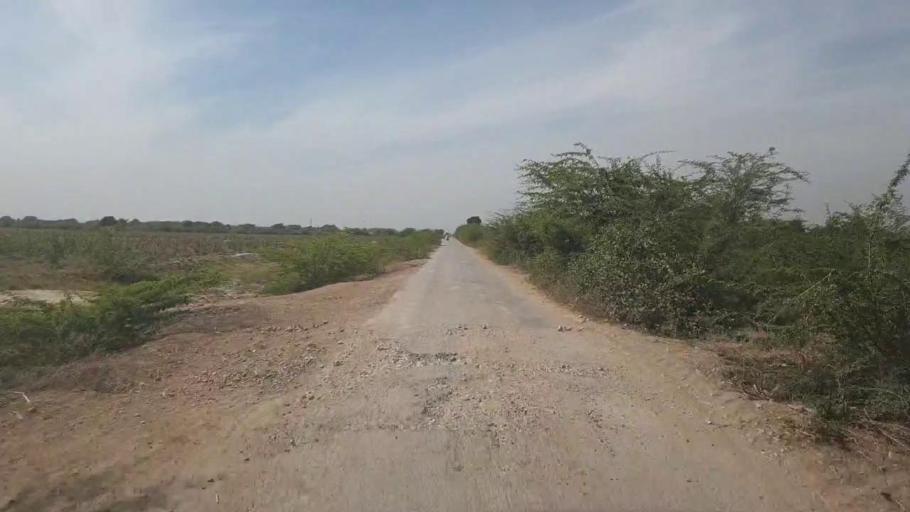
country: PK
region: Sindh
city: Kunri
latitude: 25.2120
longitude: 69.6085
